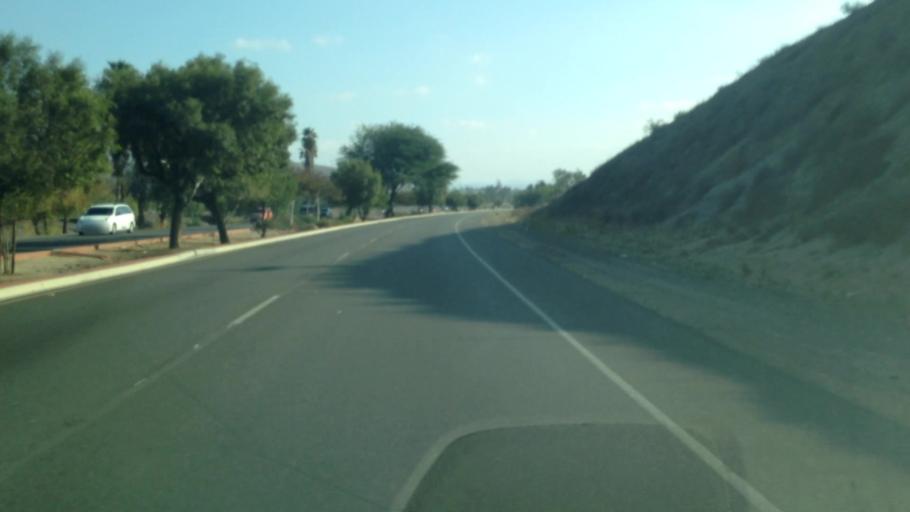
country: US
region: California
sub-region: Riverside County
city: Glen Avon
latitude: 33.9944
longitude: -117.4831
